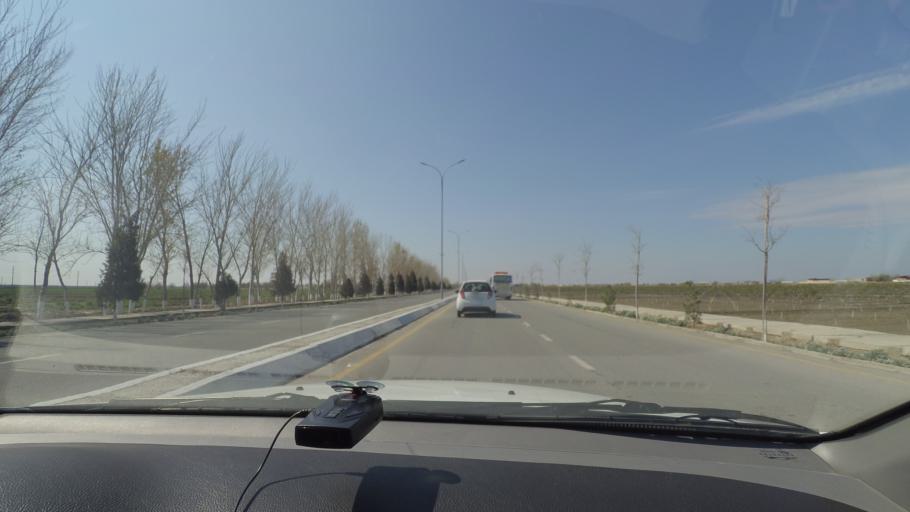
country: UZ
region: Bukhara
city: Bukhara
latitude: 39.7992
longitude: 64.4850
